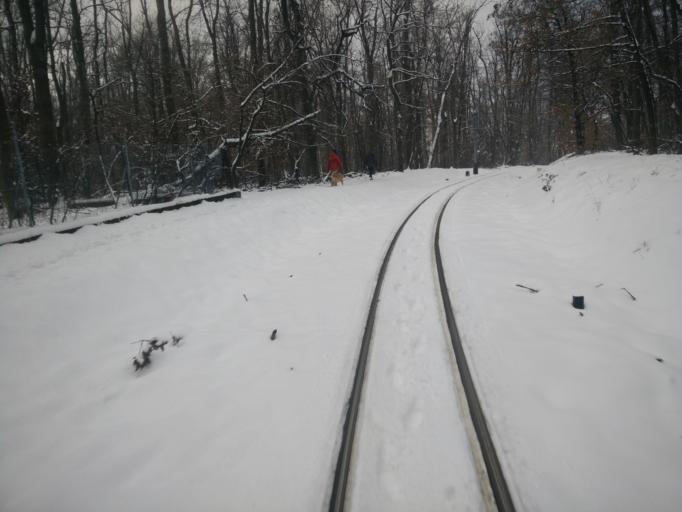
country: HU
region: Pest
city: Budakeszi
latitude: 47.4983
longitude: 18.9590
